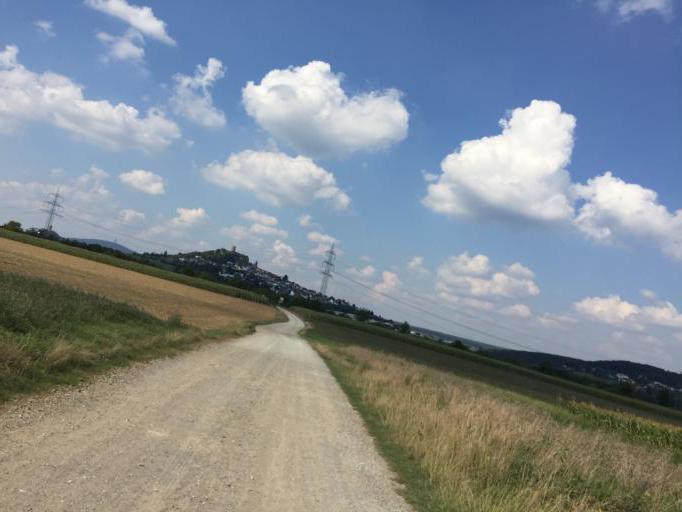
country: DE
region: Hesse
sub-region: Regierungsbezirk Giessen
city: Heuchelheim
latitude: 50.6028
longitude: 8.6461
